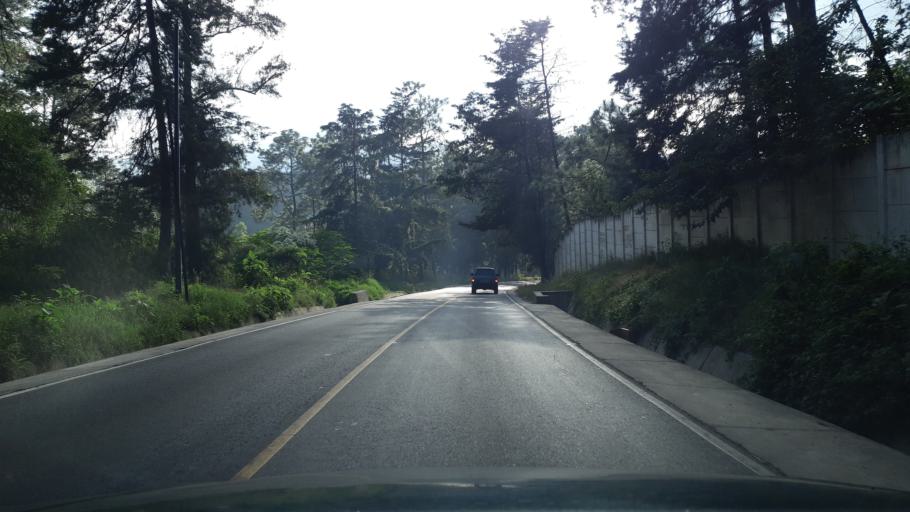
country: GT
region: Chimaltenango
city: El Tejar
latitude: 14.6382
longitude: -90.8111
